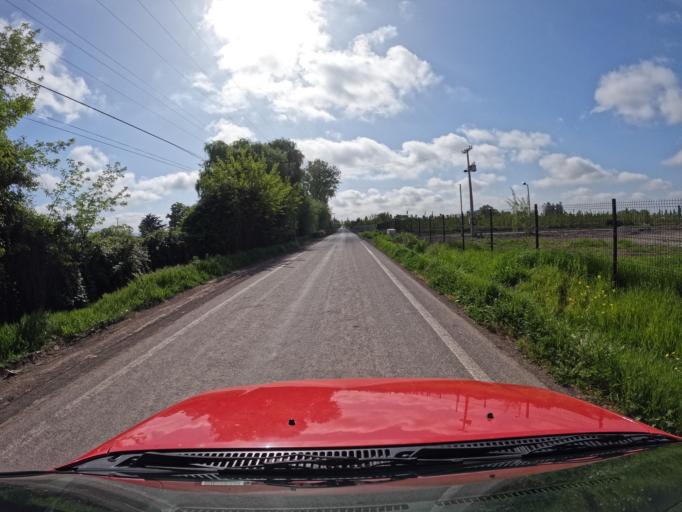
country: CL
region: Maule
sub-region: Provincia de Curico
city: Rauco
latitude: -34.8876
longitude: -71.2659
